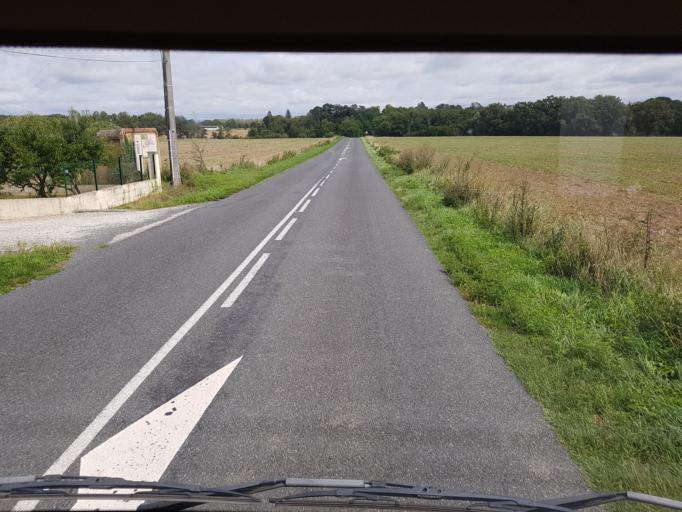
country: FR
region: Rhone-Alpes
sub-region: Departement de l'Ain
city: Beligneux
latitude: 45.9266
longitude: 5.1148
